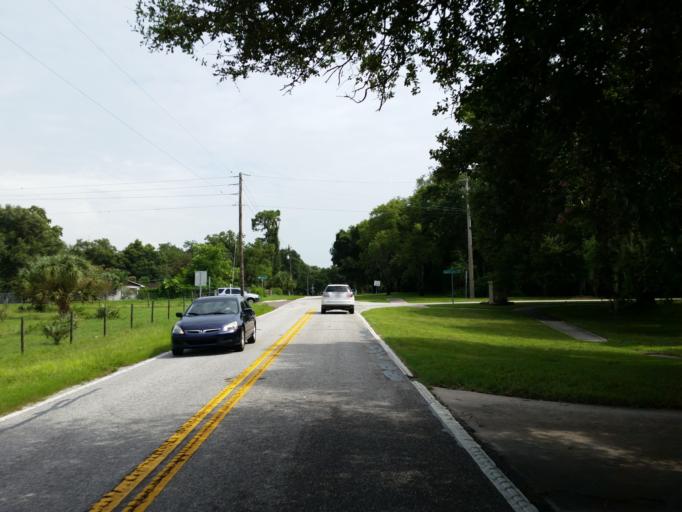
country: US
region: Florida
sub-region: Hillsborough County
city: Bloomingdale
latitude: 27.9076
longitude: -82.2528
